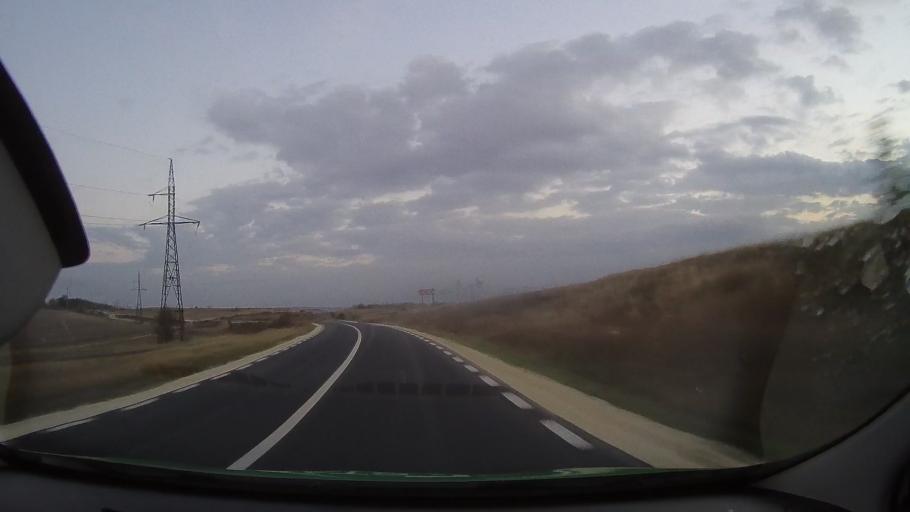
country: RO
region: Constanta
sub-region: Comuna Baneasa
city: Baneasa
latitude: 44.0820
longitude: 27.6888
